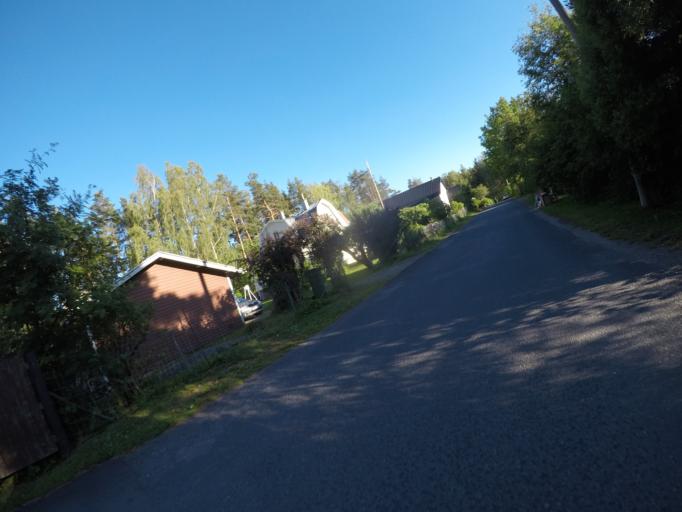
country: FI
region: Haeme
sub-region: Haemeenlinna
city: Haemeenlinna
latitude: 60.9834
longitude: 24.4534
